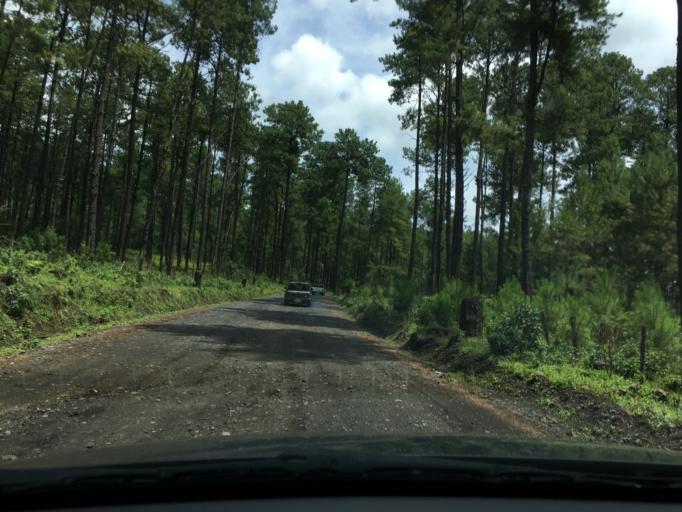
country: MX
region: Michoacan
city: Nuevo San Juan Parangaricutiro
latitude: 19.4444
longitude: -102.1797
